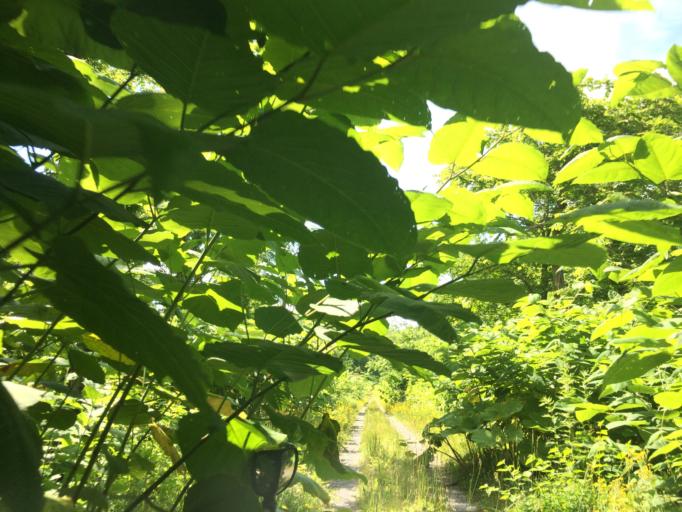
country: JP
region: Hokkaido
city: Niseko Town
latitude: 42.8646
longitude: 140.7909
